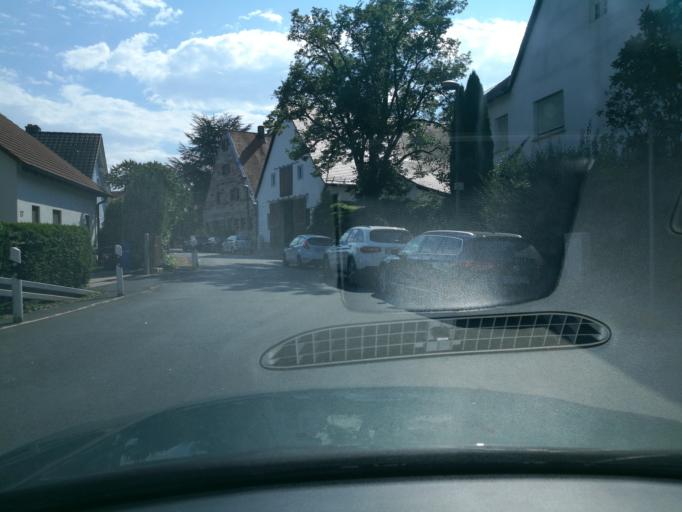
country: DE
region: Bavaria
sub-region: Regierungsbezirk Mittelfranken
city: Furth
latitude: 49.5119
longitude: 10.9550
